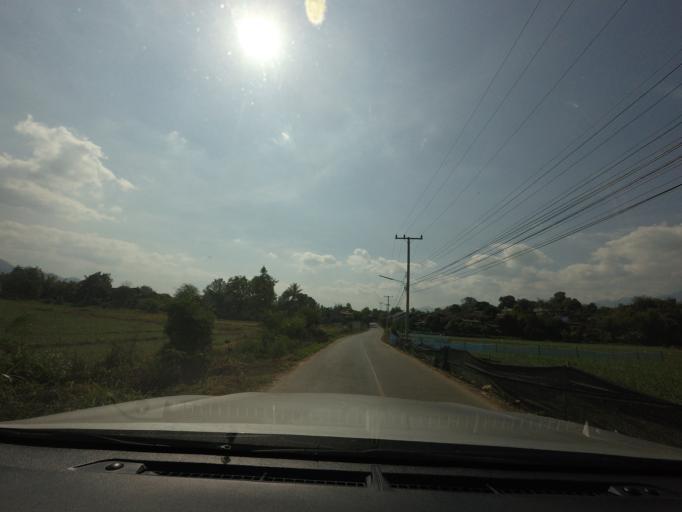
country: TH
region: Mae Hong Son
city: Wiang Nuea
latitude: 19.3871
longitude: 98.4410
